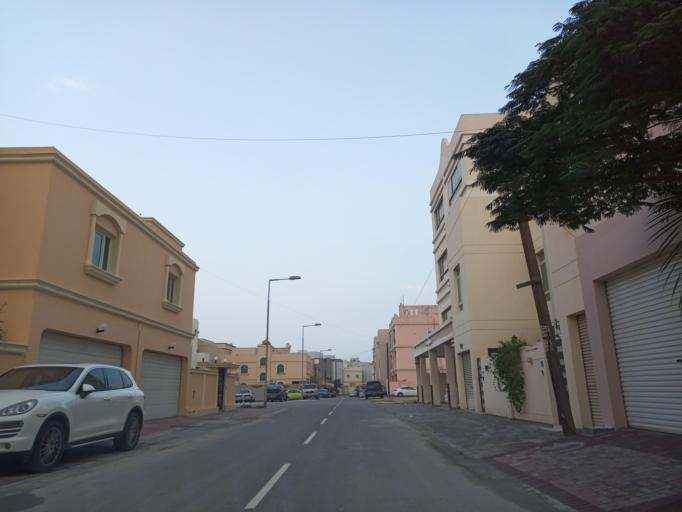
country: BH
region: Muharraq
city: Al Hadd
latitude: 26.2382
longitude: 50.6499
